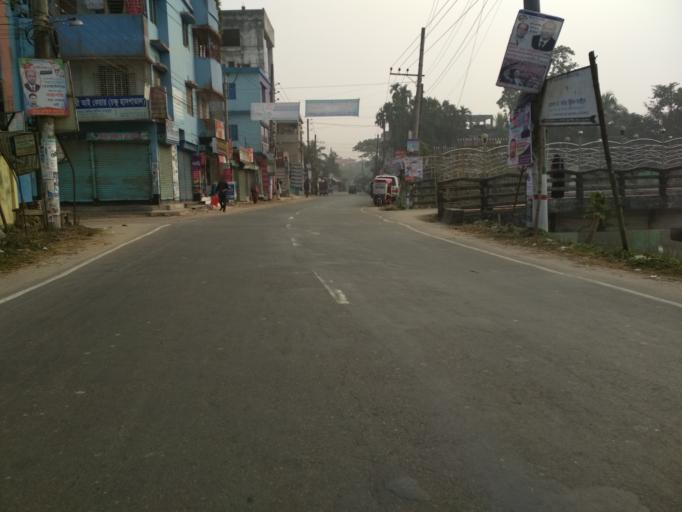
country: BD
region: Chittagong
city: Lakshmipur
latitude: 22.9398
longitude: 90.8414
